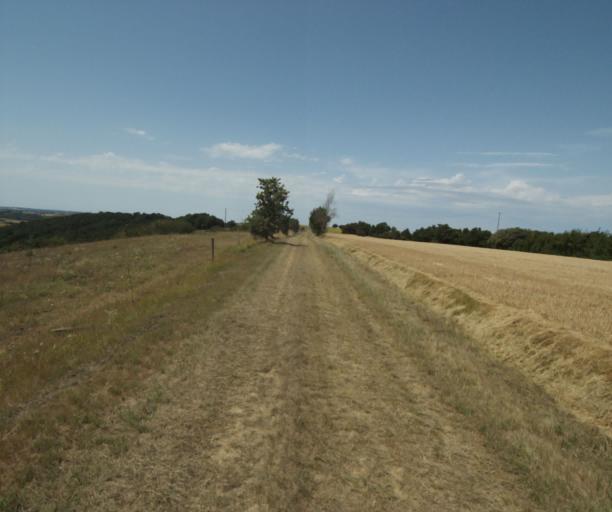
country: FR
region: Midi-Pyrenees
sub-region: Departement de la Haute-Garonne
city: Saint-Felix-Lauragais
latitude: 43.4440
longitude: 1.8651
